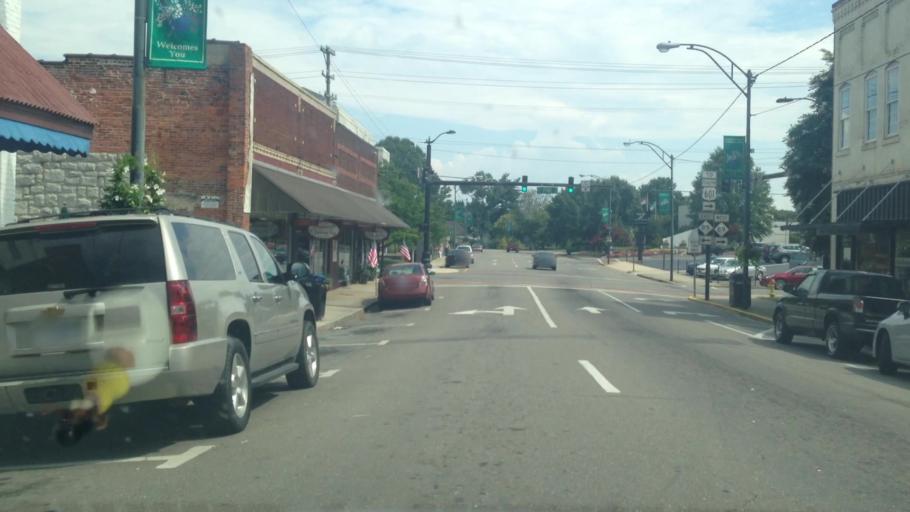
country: US
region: North Carolina
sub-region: Surry County
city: Mount Airy
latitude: 36.4998
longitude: -80.6073
